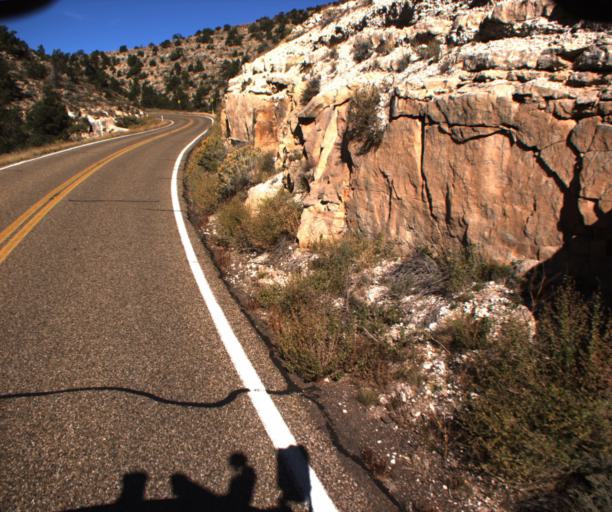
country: US
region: Arizona
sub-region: Coconino County
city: Fredonia
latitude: 36.7248
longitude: -112.0815
